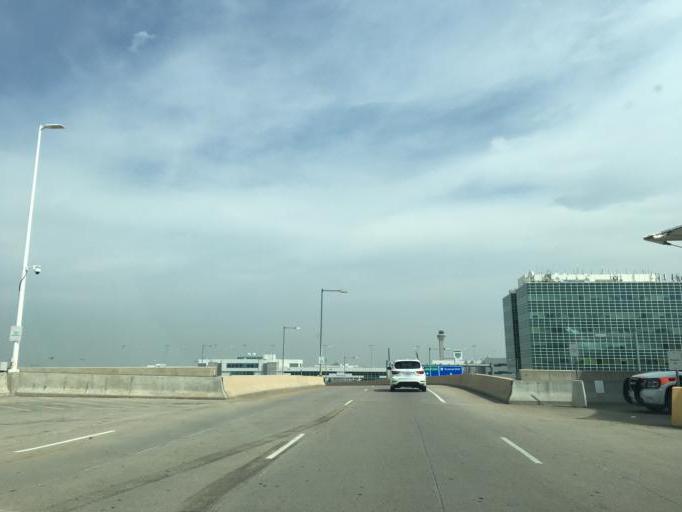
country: US
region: Colorado
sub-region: Weld County
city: Lochbuie
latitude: 39.8503
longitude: -104.6750
